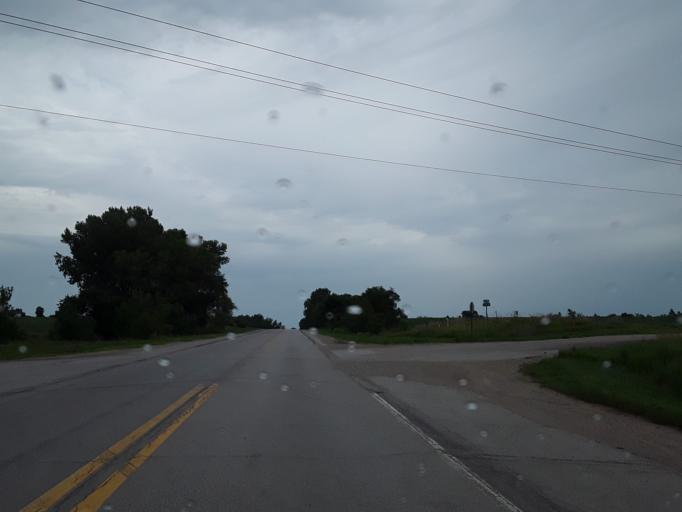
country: US
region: Nebraska
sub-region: Washington County
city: Blair
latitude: 41.5088
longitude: -96.1555
